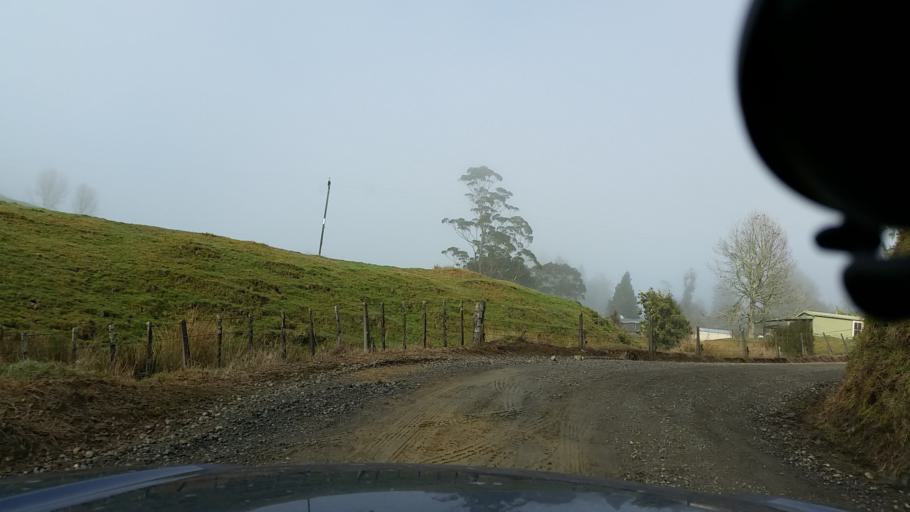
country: NZ
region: Taranaki
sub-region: New Plymouth District
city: Waitara
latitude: -38.9929
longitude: 174.7759
